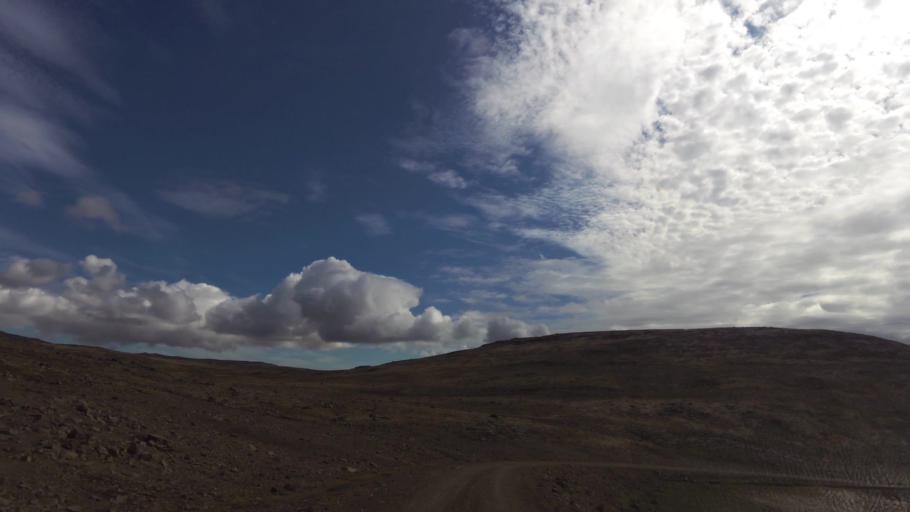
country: IS
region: West
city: Olafsvik
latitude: 65.6145
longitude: -24.3042
